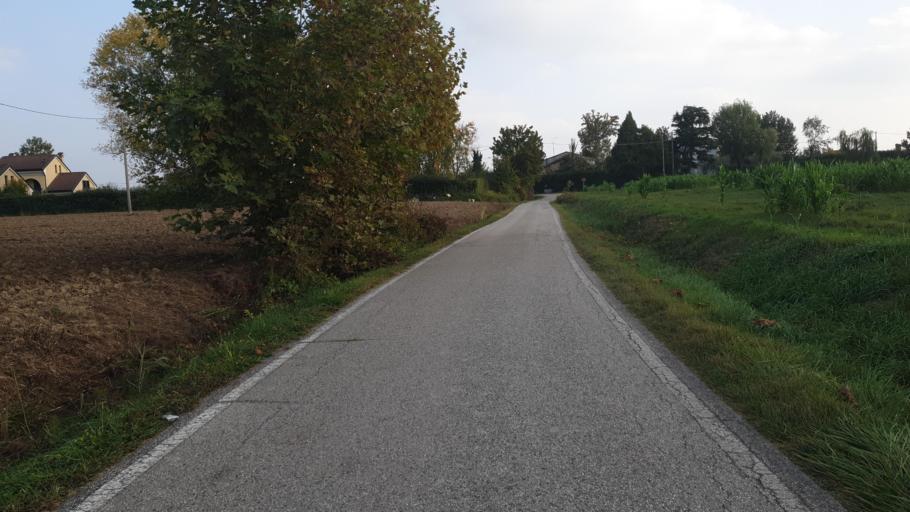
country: IT
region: Veneto
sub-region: Provincia di Padova
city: Terradura
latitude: 45.3432
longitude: 11.8093
